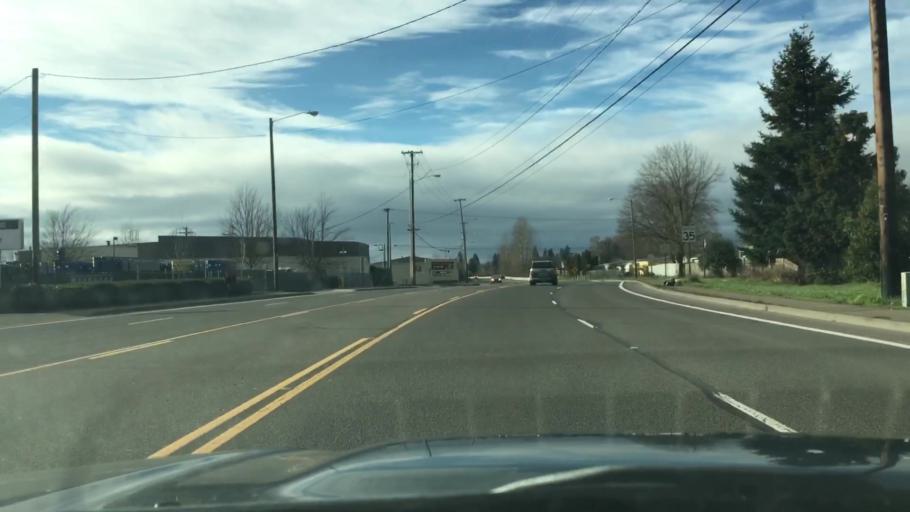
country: US
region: Oregon
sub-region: Lane County
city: Eugene
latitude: 44.0638
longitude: -123.1409
